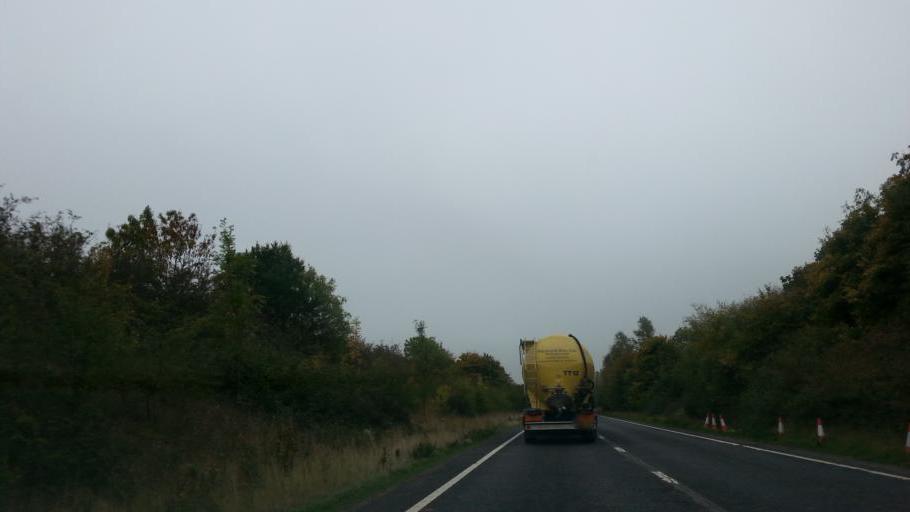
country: GB
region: England
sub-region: Northamptonshire
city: Thrapston
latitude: 52.3860
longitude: -0.5235
